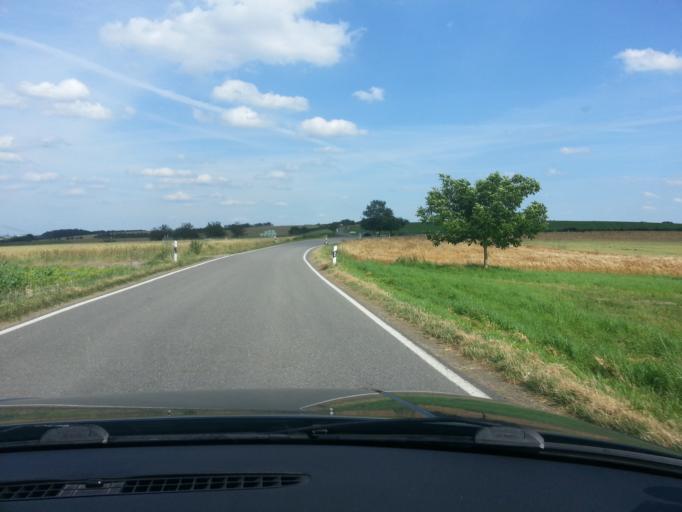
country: DE
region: Rheinland-Pfalz
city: Bottenbach
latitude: 49.1890
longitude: 7.4879
